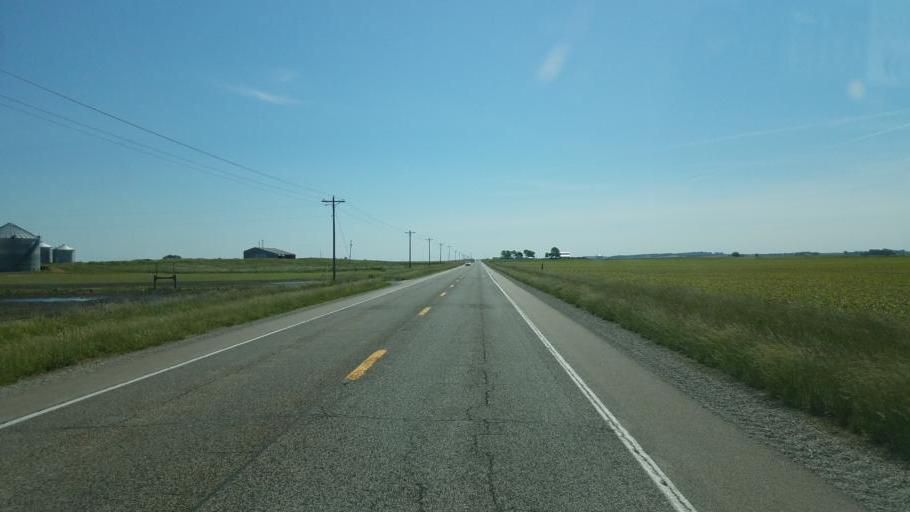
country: US
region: Illinois
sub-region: Mason County
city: Manito
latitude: 40.3037
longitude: -89.7680
